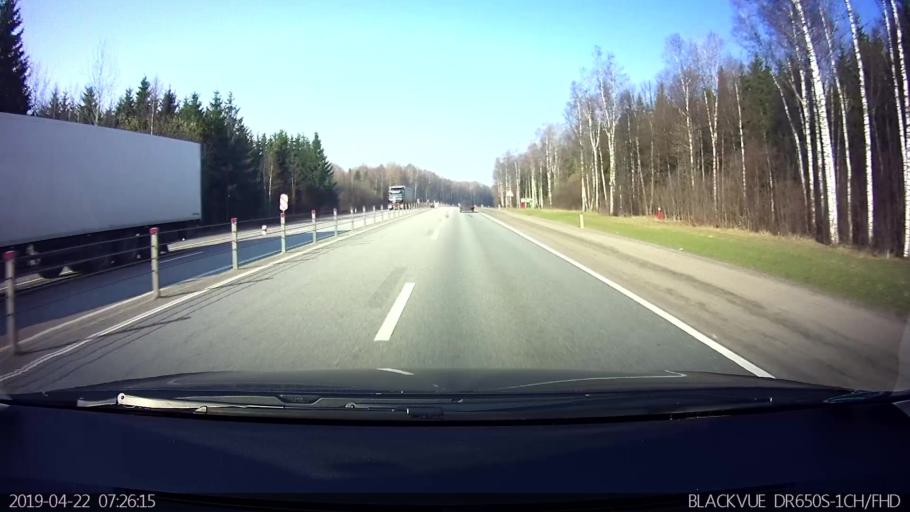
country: RU
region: Smolensk
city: Vyaz'ma
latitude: 55.1886
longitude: 34.0655
